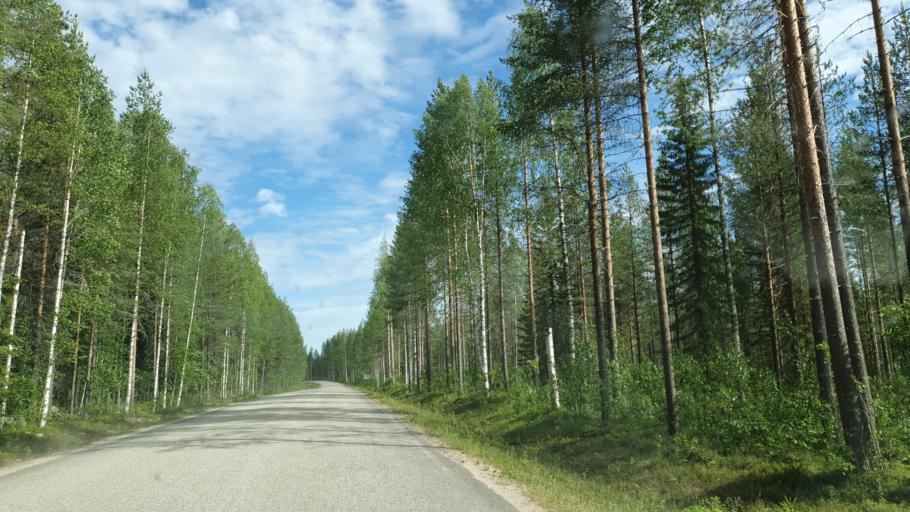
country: FI
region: Kainuu
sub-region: Kehys-Kainuu
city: Kuhmo
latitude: 64.5172
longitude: 29.3900
